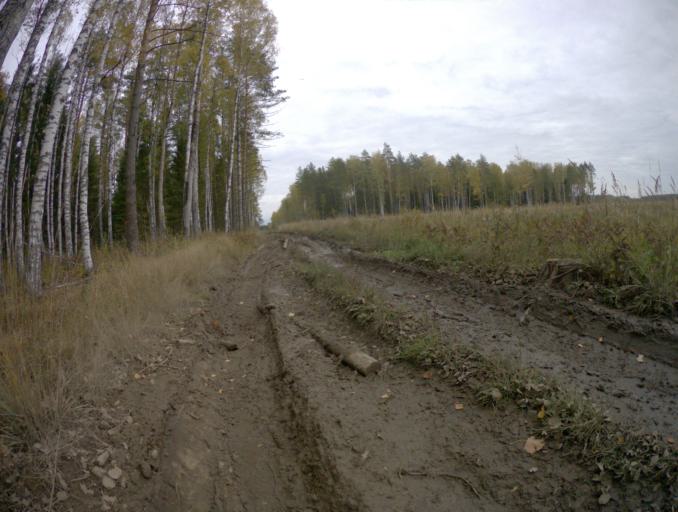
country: RU
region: Vladimir
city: Stepantsevo
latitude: 56.3160
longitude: 41.5542
